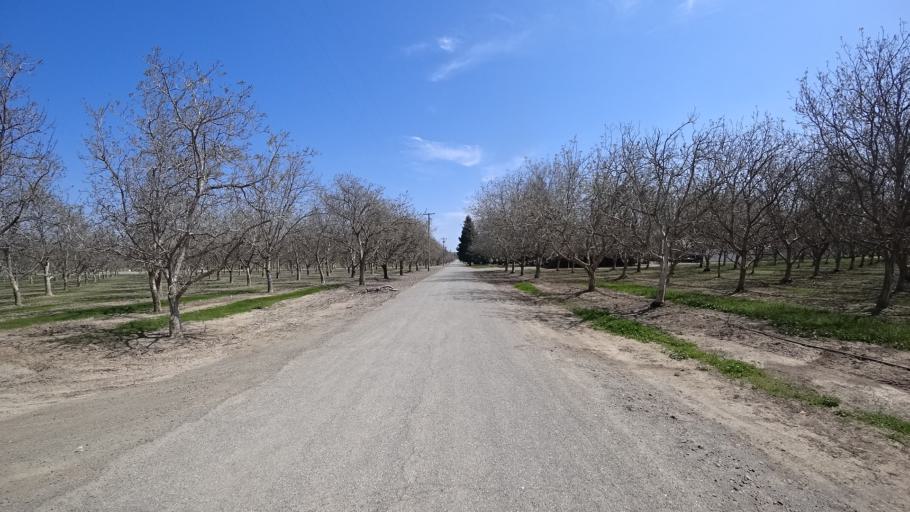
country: US
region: California
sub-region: Glenn County
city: Willows
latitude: 39.5037
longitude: -122.0147
